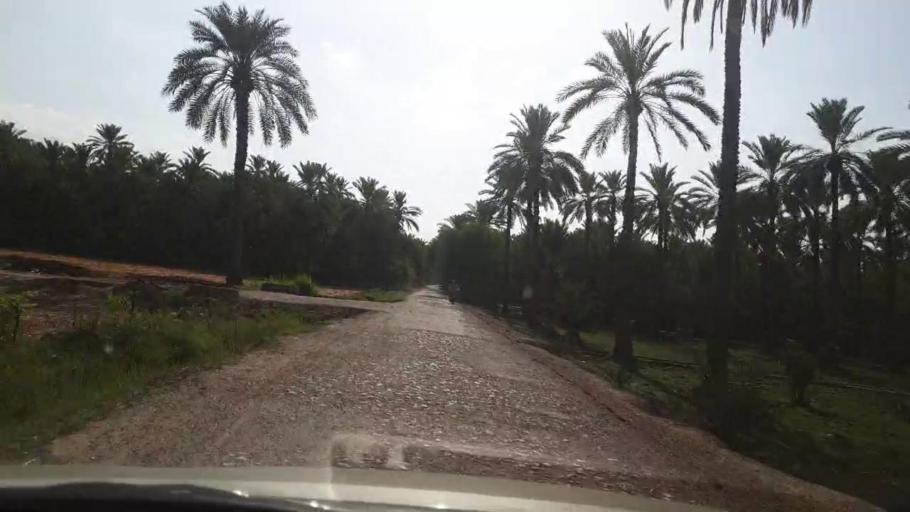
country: PK
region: Sindh
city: Sukkur
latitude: 27.6421
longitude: 68.8138
